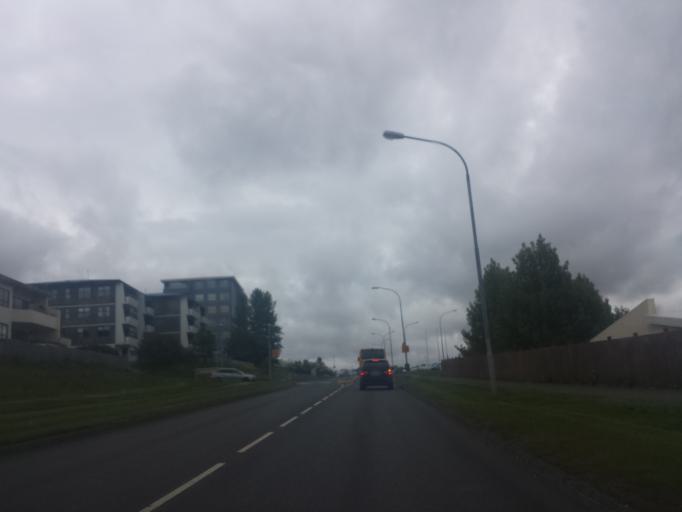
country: IS
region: Capital Region
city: Reykjavik
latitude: 64.1354
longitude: -21.8007
